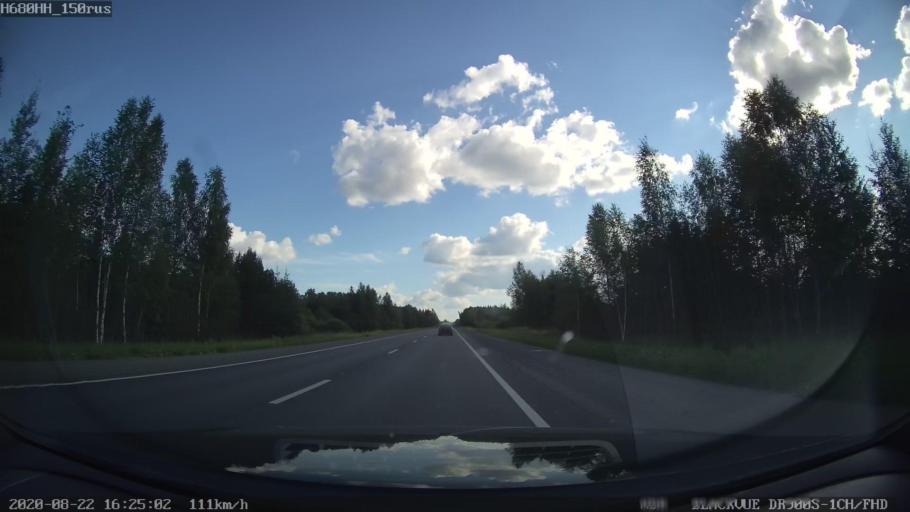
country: RU
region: Tverskaya
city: Rameshki
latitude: 57.3274
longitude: 36.0921
